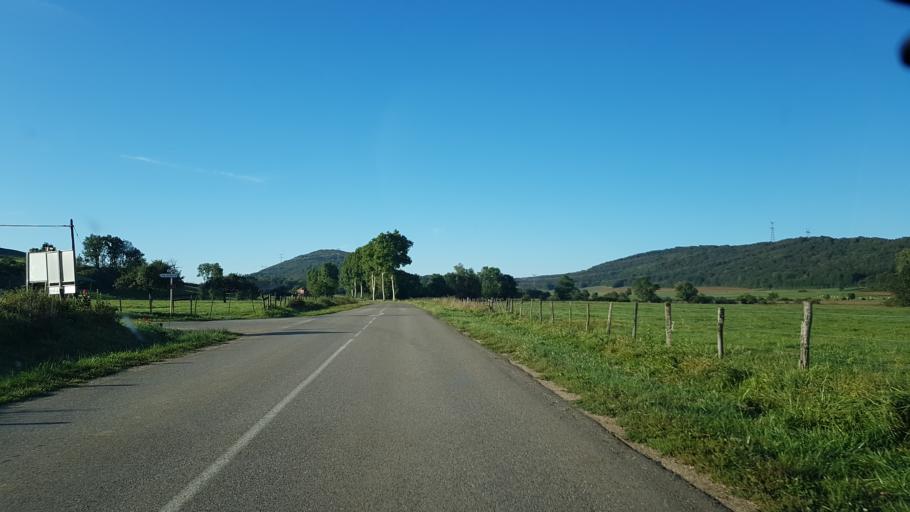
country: FR
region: Bourgogne
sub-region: Departement de Saone-et-Loire
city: Cuiseaux
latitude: 46.4487
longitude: 5.4581
